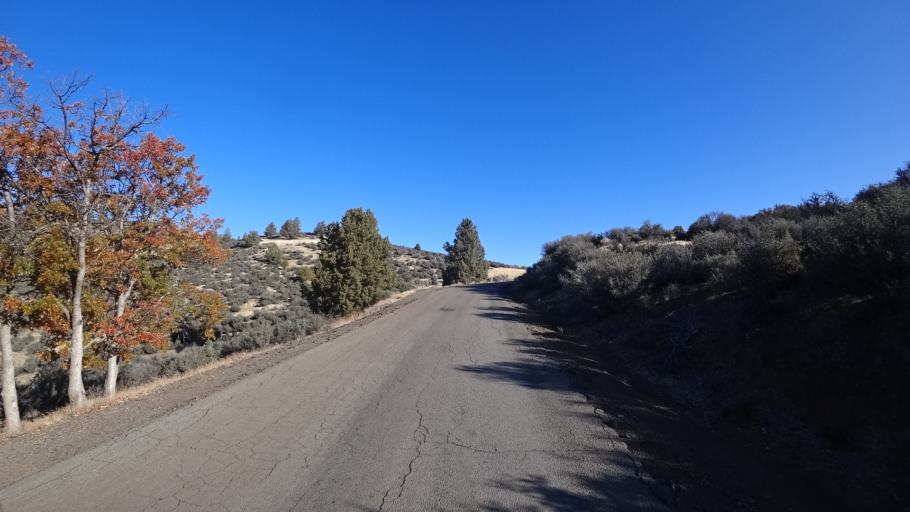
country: US
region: California
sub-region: Siskiyou County
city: Montague
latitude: 41.8785
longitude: -122.4592
